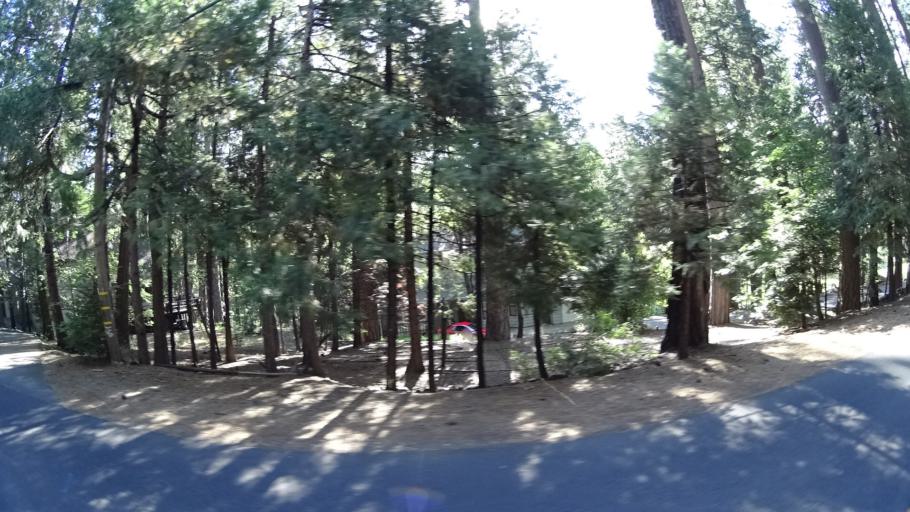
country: US
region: California
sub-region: Calaveras County
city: Arnold
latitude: 38.2563
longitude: -120.3300
